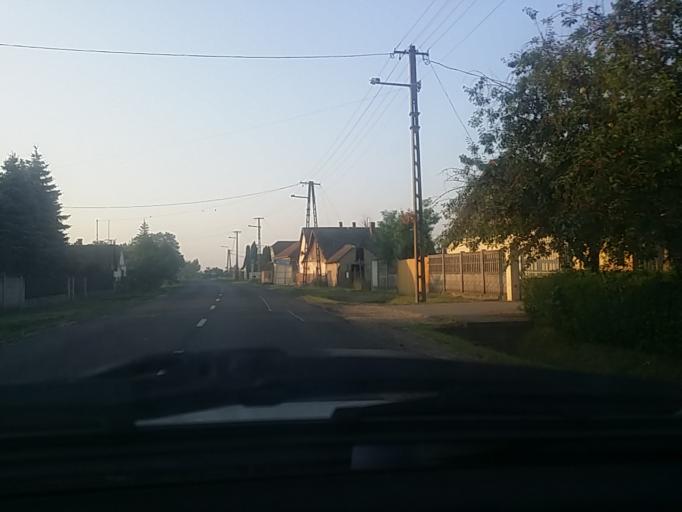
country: HU
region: Pest
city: Szentmartonkata
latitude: 47.4490
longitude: 19.7088
